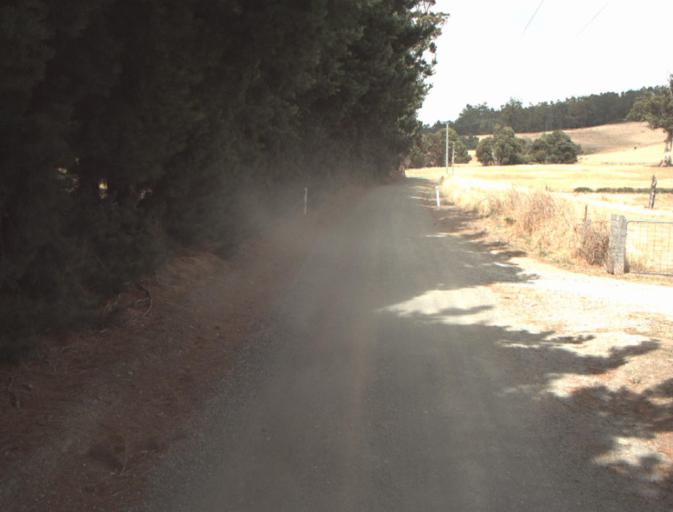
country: AU
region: Tasmania
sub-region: Launceston
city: Mayfield
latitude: -41.1728
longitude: 147.2125
